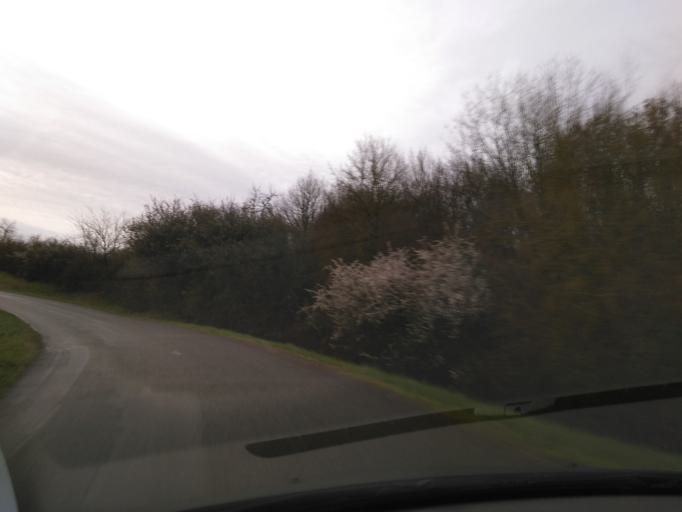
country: FR
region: Midi-Pyrenees
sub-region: Departement du Tarn-et-Garonne
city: Finhan
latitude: 43.8786
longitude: 1.1461
